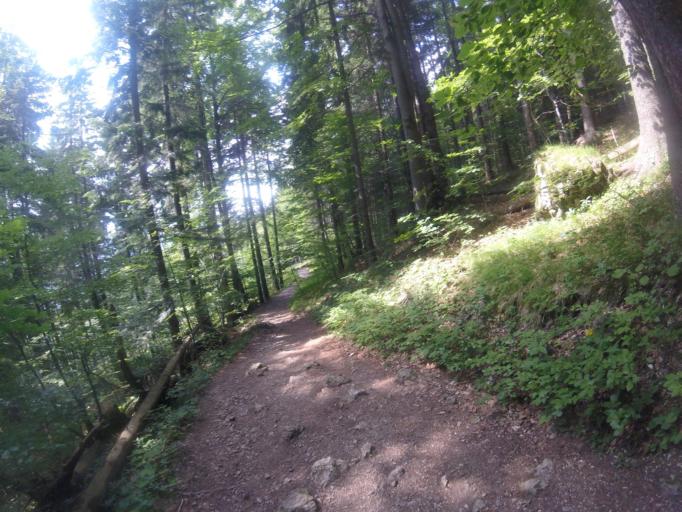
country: SK
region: Zilinsky
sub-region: Okres Zilina
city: Terchova
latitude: 49.2288
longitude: 19.0862
